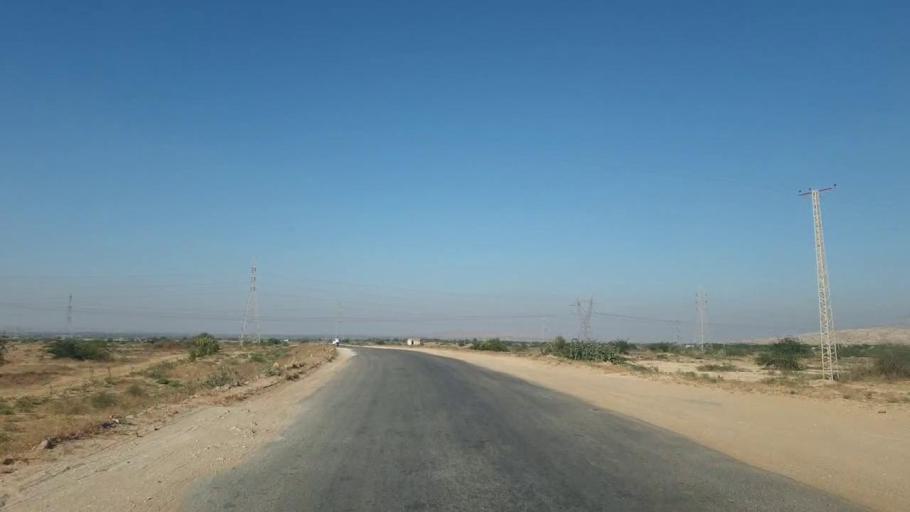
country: PK
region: Sindh
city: Gharo
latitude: 25.1719
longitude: 67.6602
